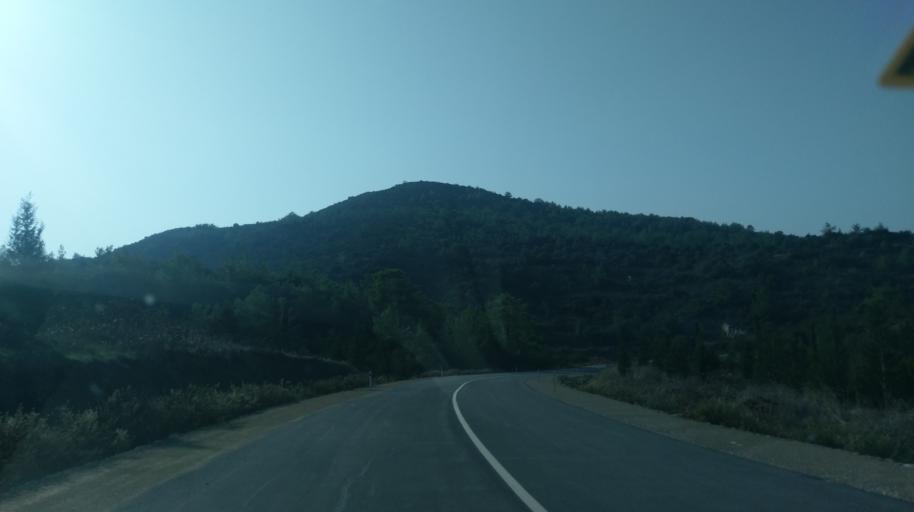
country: CY
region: Ammochostos
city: Leonarisso
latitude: 35.5330
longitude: 34.2470
